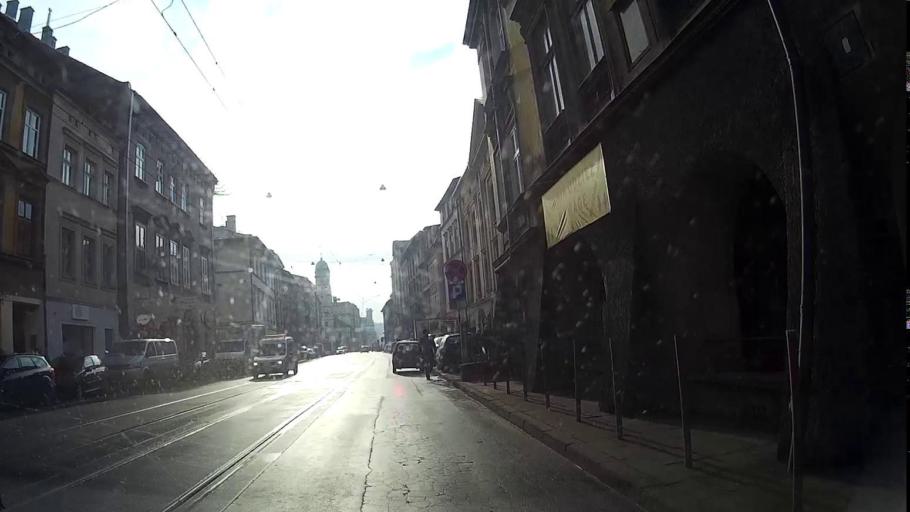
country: PL
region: Lesser Poland Voivodeship
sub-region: Krakow
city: Krakow
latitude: 50.0507
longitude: 19.9426
